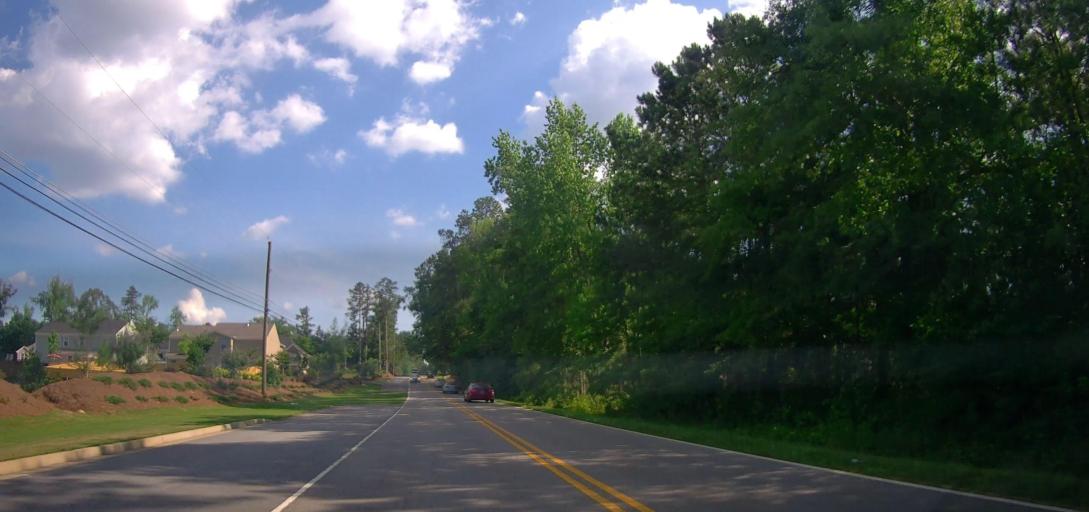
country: US
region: Georgia
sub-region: Henry County
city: Hampton
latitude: 33.4538
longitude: -84.2315
